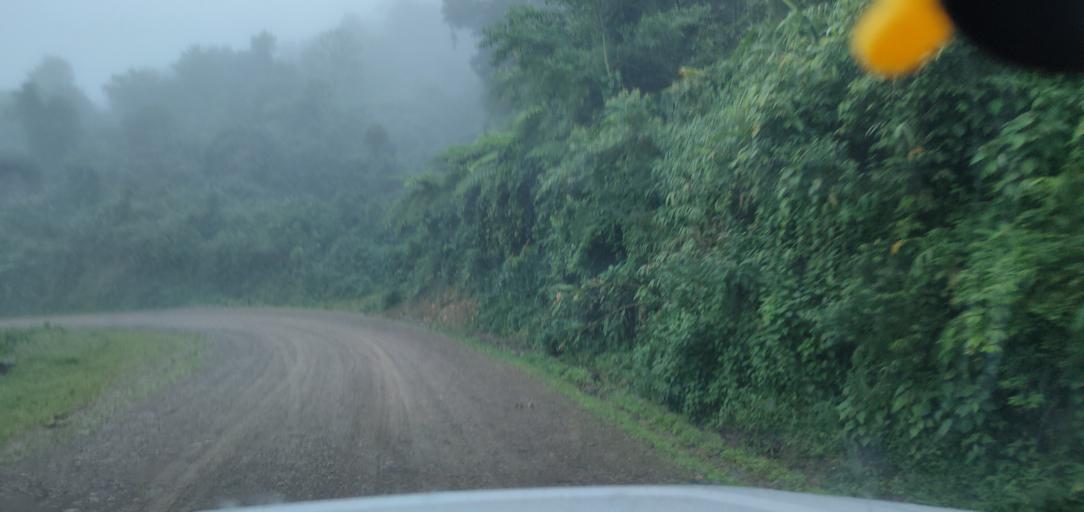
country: LA
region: Phongsali
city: Phongsali
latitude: 21.3902
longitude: 102.1960
